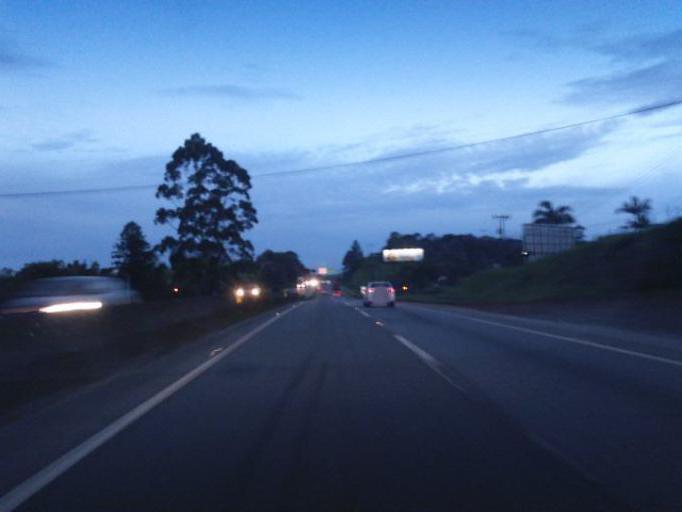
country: BR
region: Santa Catarina
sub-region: Joinville
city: Joinville
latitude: -26.4415
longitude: -48.7998
